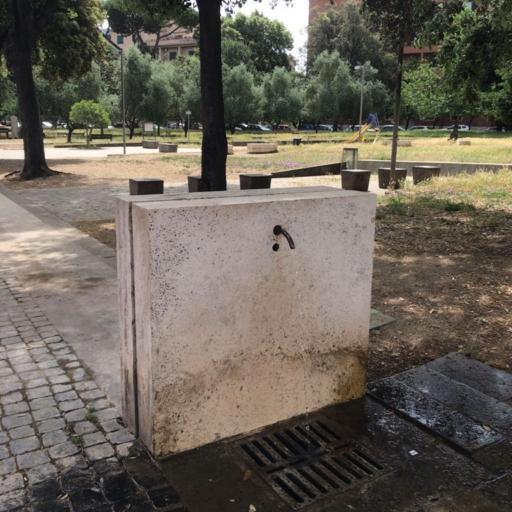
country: IT
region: Latium
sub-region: Citta metropolitana di Roma Capitale
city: Rome
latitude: 41.8602
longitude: 12.4917
